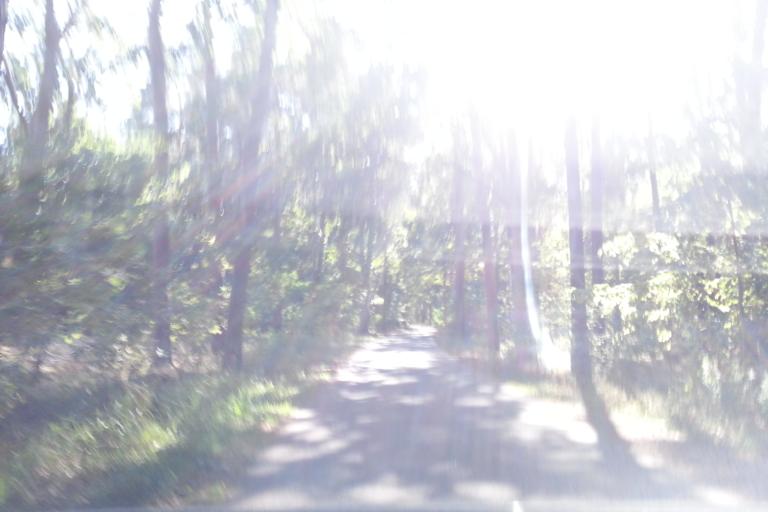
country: DE
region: Mecklenburg-Vorpommern
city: Eggesin
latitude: 53.6912
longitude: 14.0494
